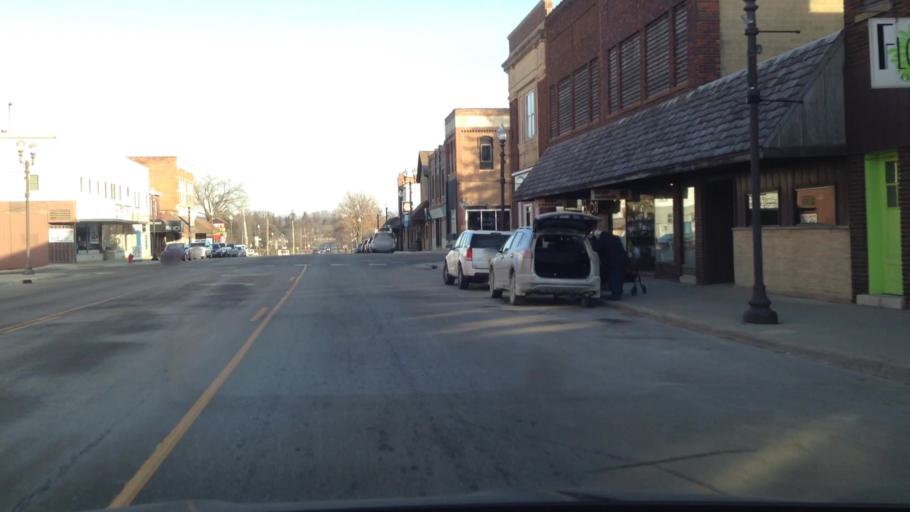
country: US
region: Minnesota
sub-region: Goodhue County
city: Zumbrota
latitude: 44.2937
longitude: -92.6691
